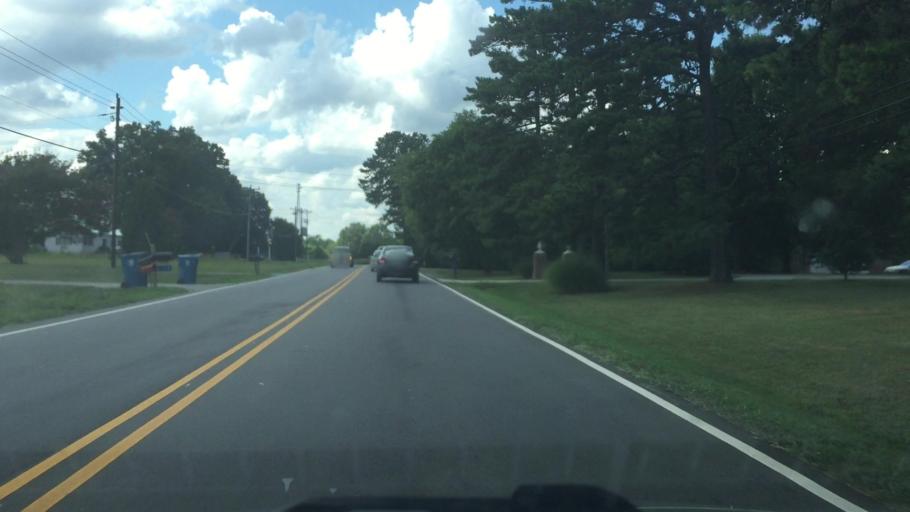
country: US
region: North Carolina
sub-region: Rowan County
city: Enochville
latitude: 35.4429
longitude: -80.7286
